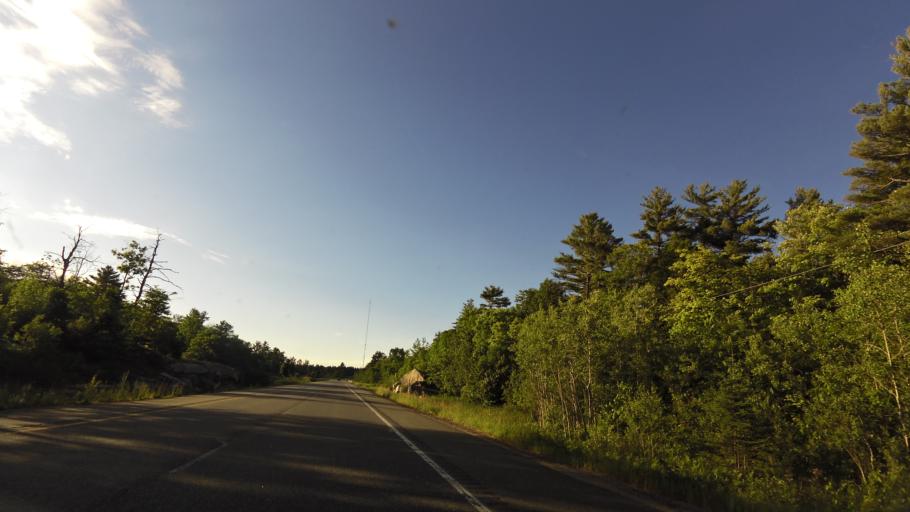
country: CA
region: Ontario
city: Midland
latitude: 44.9520
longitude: -79.7770
